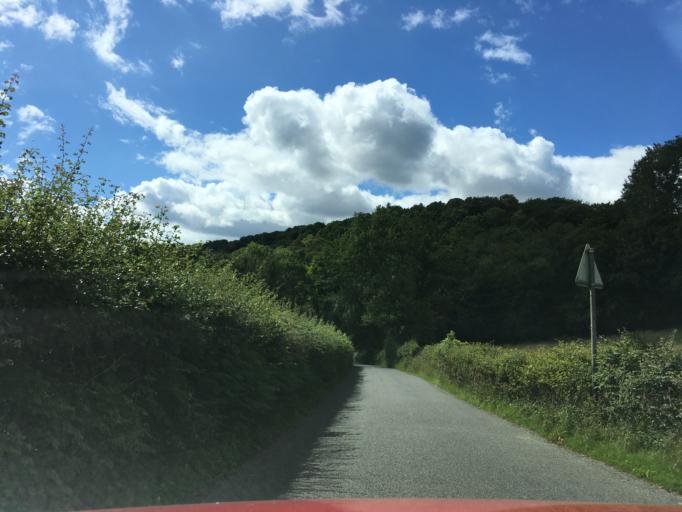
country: GB
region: England
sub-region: Gloucestershire
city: Bream
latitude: 51.7438
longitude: -2.5579
